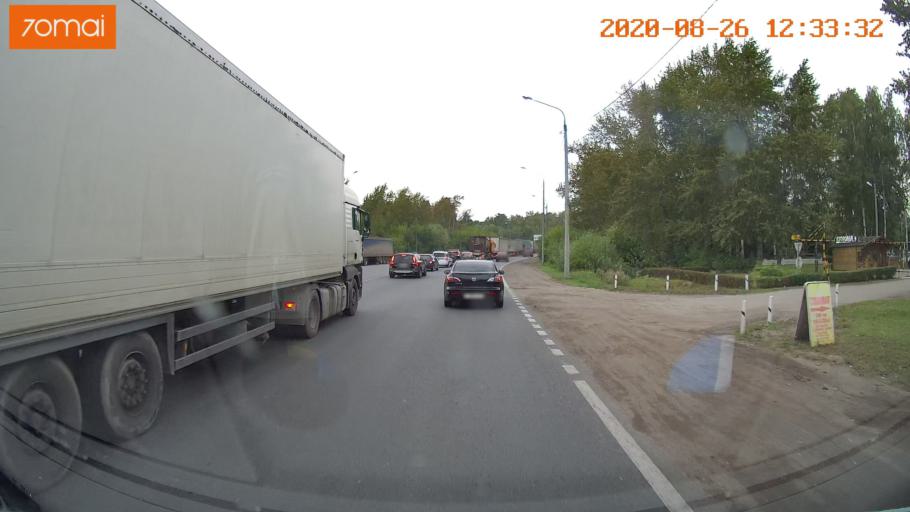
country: RU
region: Rjazan
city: Ryazan'
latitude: 54.5823
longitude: 39.7756
